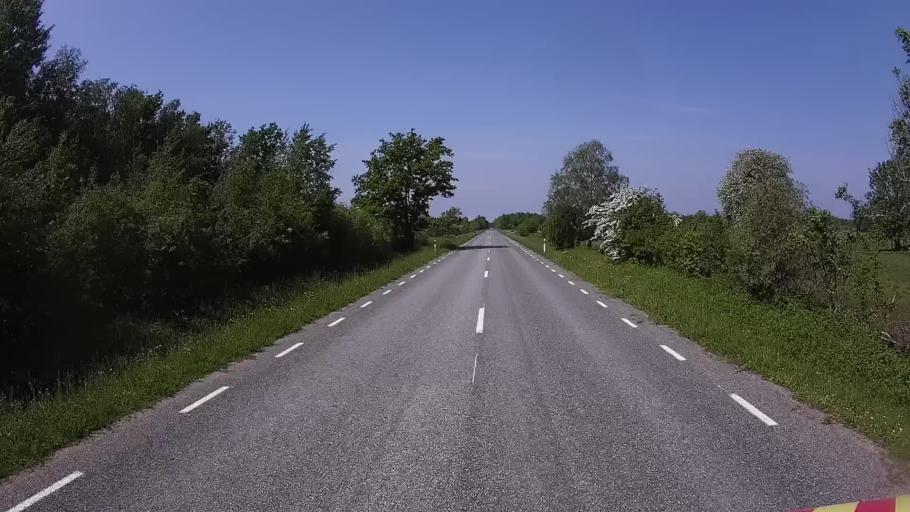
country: EE
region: Saare
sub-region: Kuressaare linn
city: Kuressaare
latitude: 58.3672
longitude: 22.0515
